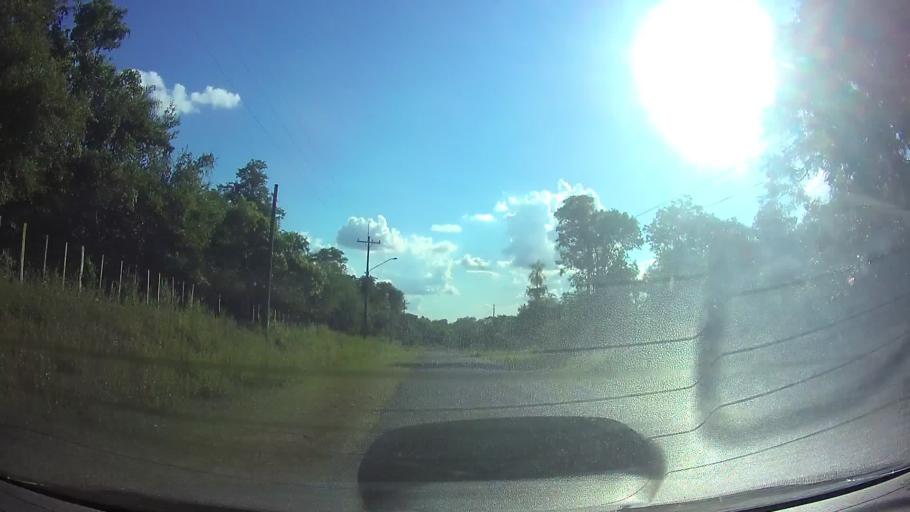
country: PY
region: Central
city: Aregua
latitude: -25.3325
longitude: -57.3780
